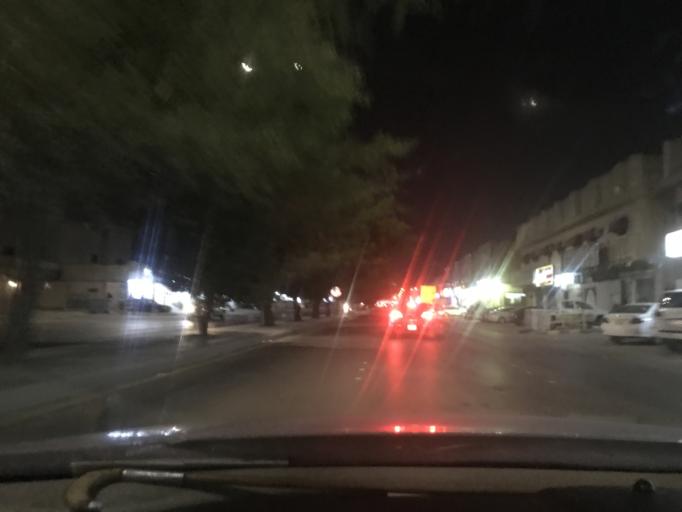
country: SA
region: Ar Riyad
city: Riyadh
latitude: 24.7383
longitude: 46.7765
